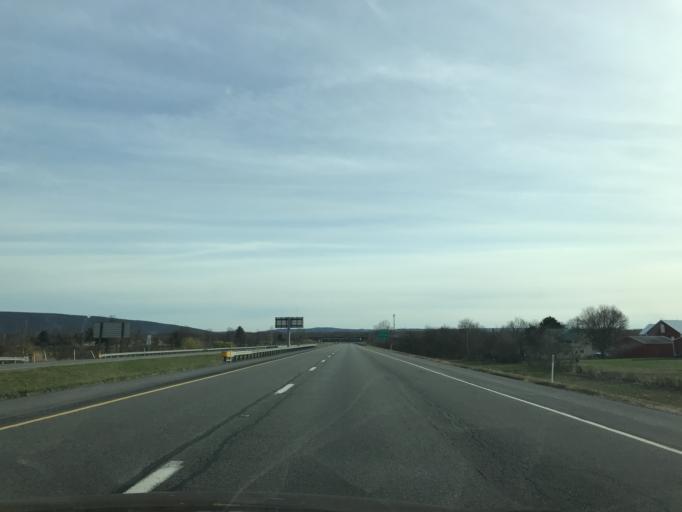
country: US
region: Pennsylvania
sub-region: Northumberland County
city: Milton
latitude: 41.0028
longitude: -76.8325
